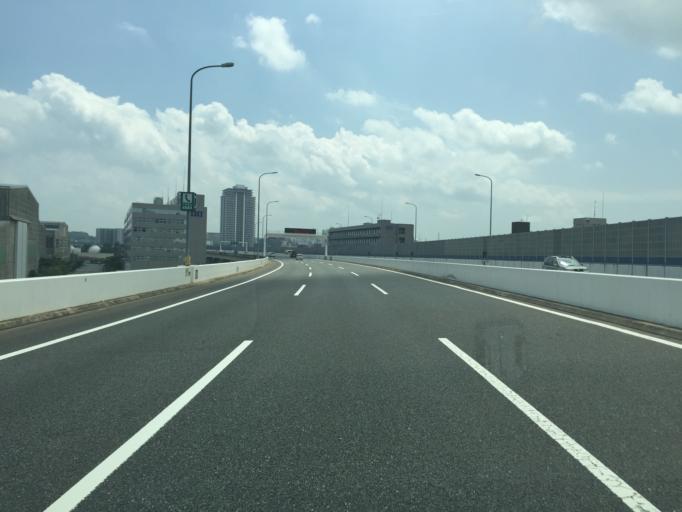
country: JP
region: Kanagawa
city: Yokohama
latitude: 35.3932
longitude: 139.6163
